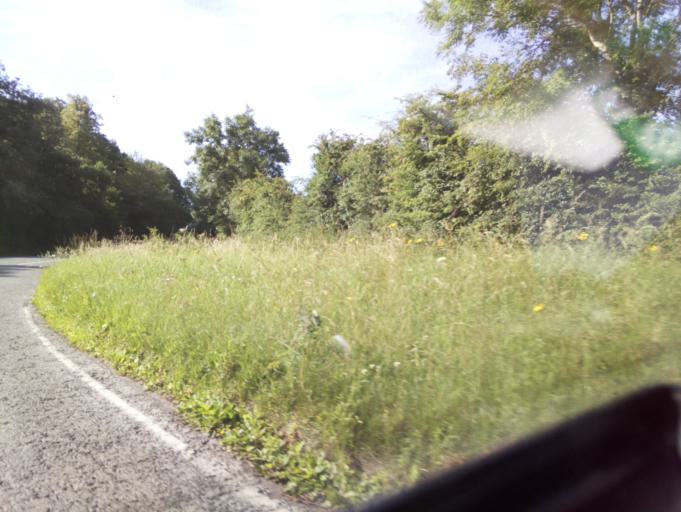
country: GB
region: England
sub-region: South Gloucestershire
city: Pucklechurch
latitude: 51.4431
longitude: -2.4153
